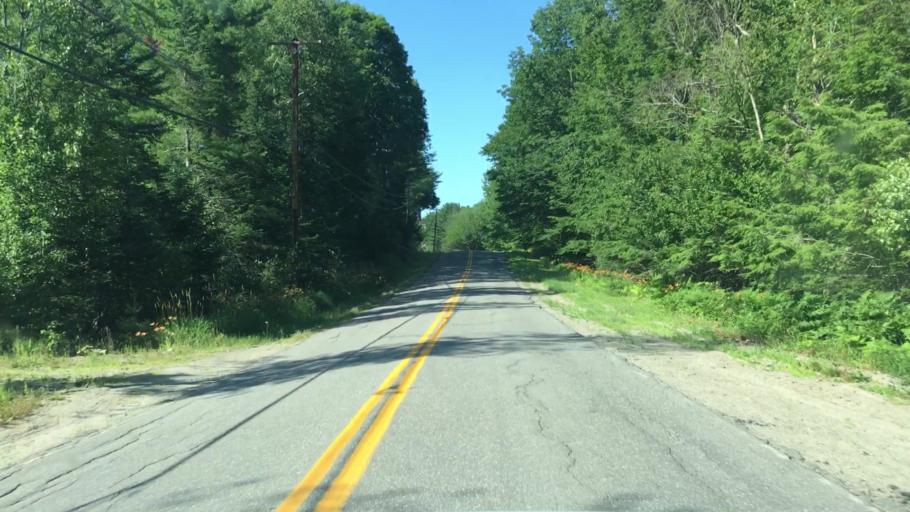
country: US
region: Maine
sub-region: Penobscot County
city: Enfield
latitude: 45.2533
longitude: -68.5649
